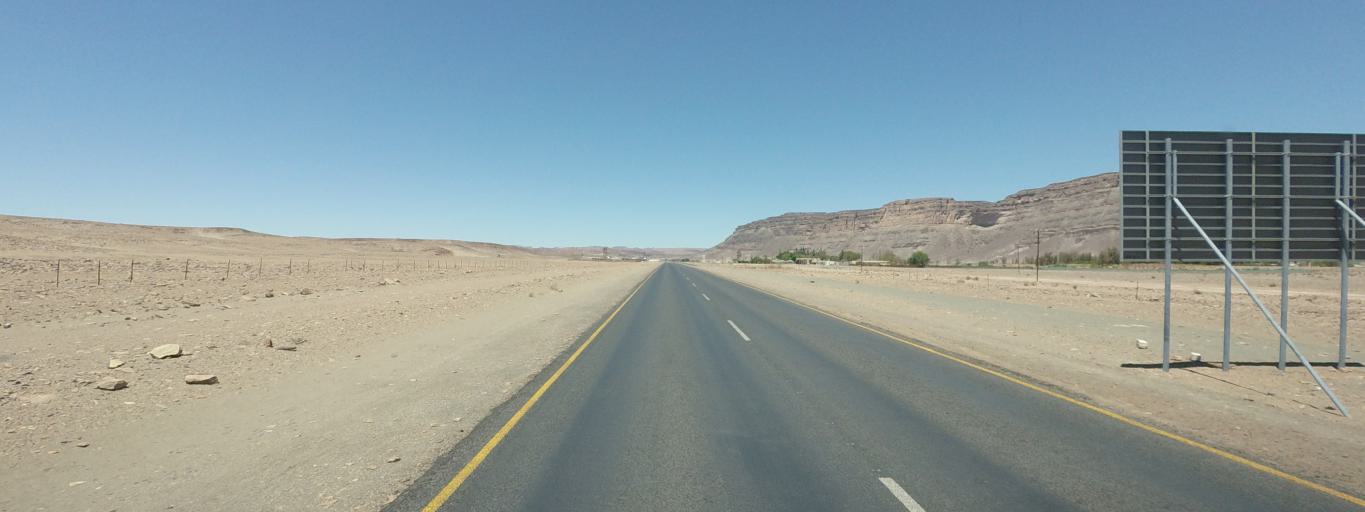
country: ZA
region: Northern Cape
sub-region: Namakwa District Municipality
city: Port Nolloth
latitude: -28.7387
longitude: 17.6174
